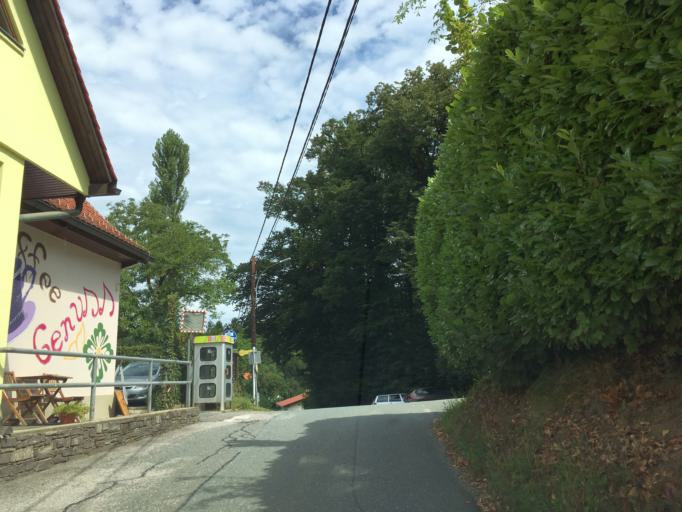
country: AT
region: Styria
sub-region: Politischer Bezirk Leibnitz
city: Kitzeck im Sausal
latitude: 46.7934
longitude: 15.4234
